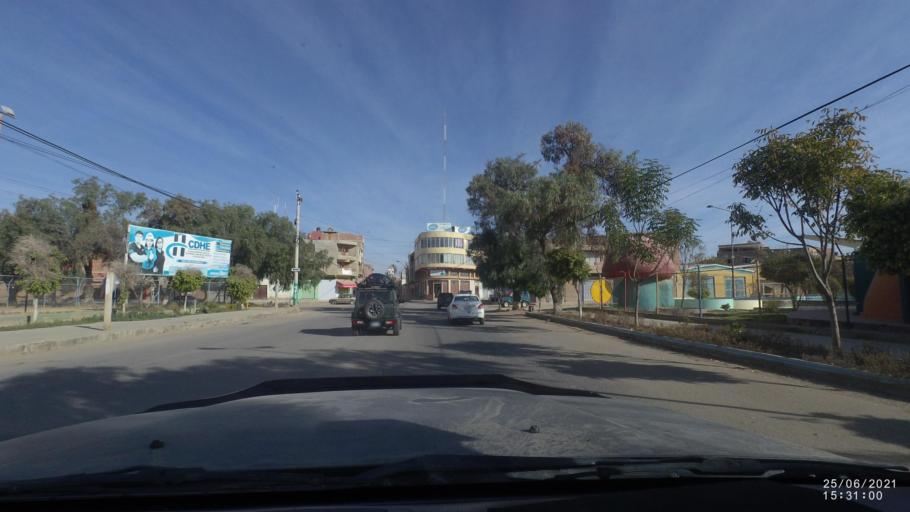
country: BO
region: Cochabamba
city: Cliza
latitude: -17.5883
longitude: -65.9340
